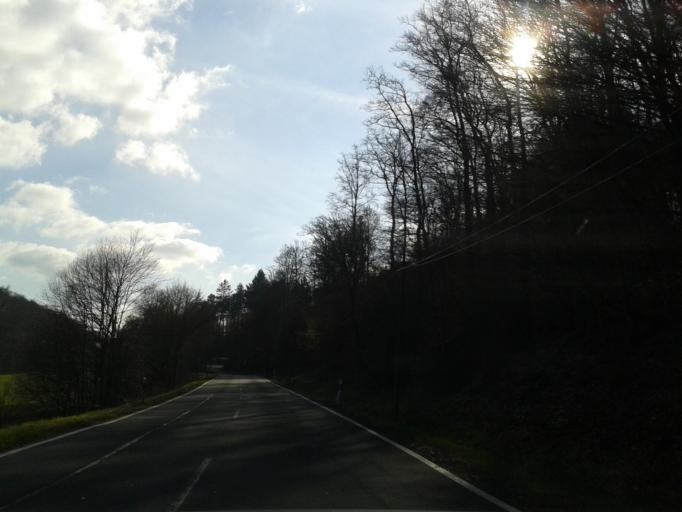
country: DE
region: Hesse
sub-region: Regierungsbezirk Giessen
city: Mittenaar
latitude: 50.7523
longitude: 8.3569
